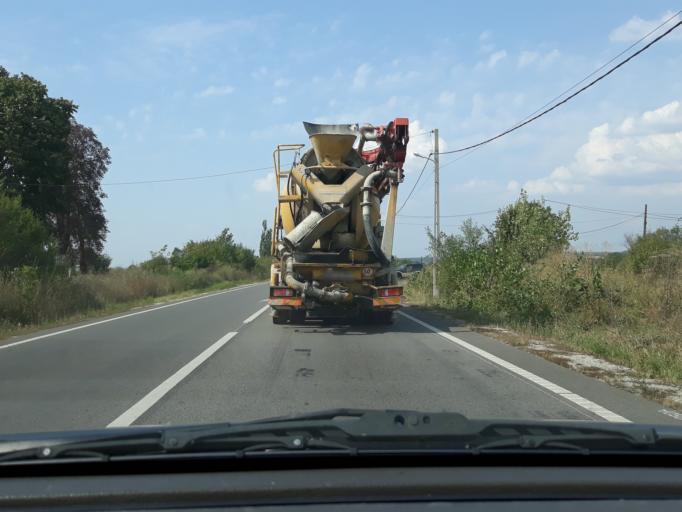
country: RO
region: Bihor
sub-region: Comuna Draganesti
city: Draganesti
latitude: 46.6334
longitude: 22.3850
